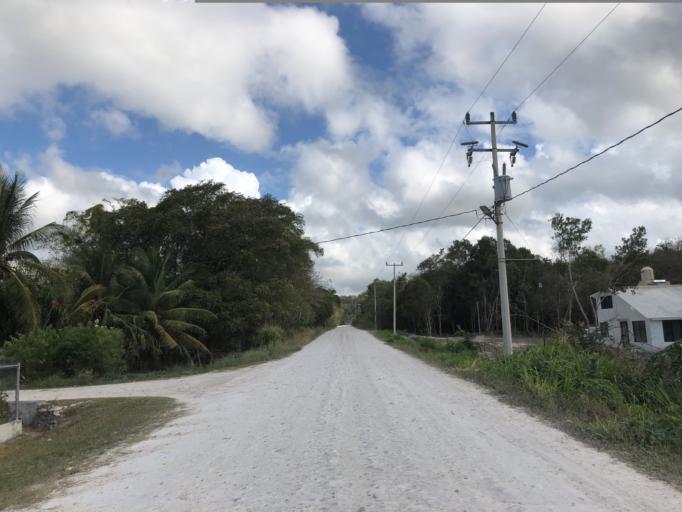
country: MX
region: Quintana Roo
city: Nicolas Bravo
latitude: 18.4559
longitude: -89.3056
